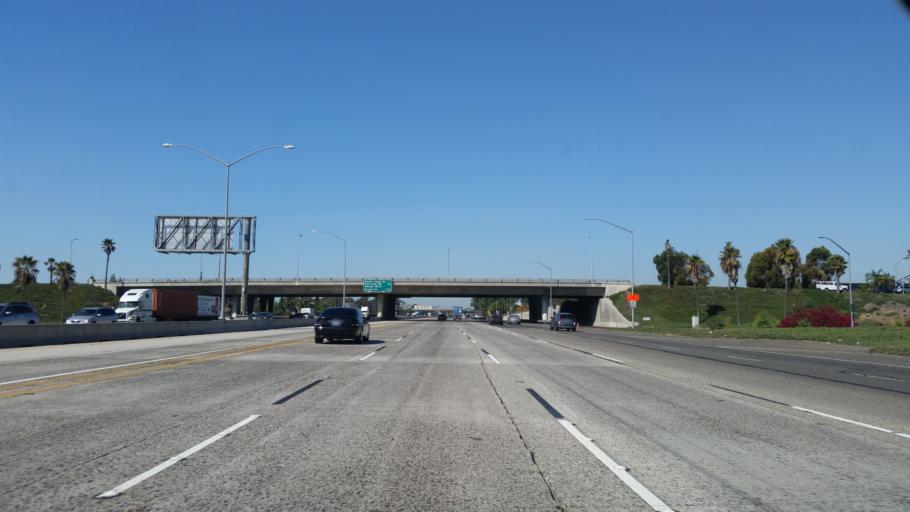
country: US
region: California
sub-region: Orange County
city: Costa Mesa
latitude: 33.6875
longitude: -117.8840
